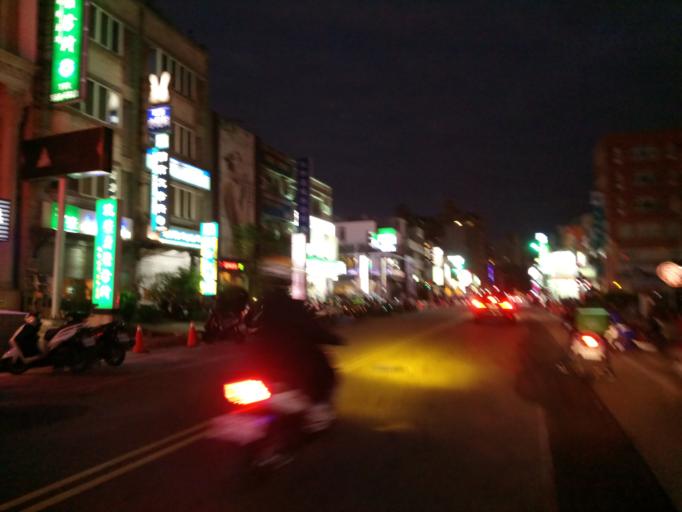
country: TW
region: Taiwan
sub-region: Hsinchu
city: Zhubei
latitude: 24.8305
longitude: 121.0147
